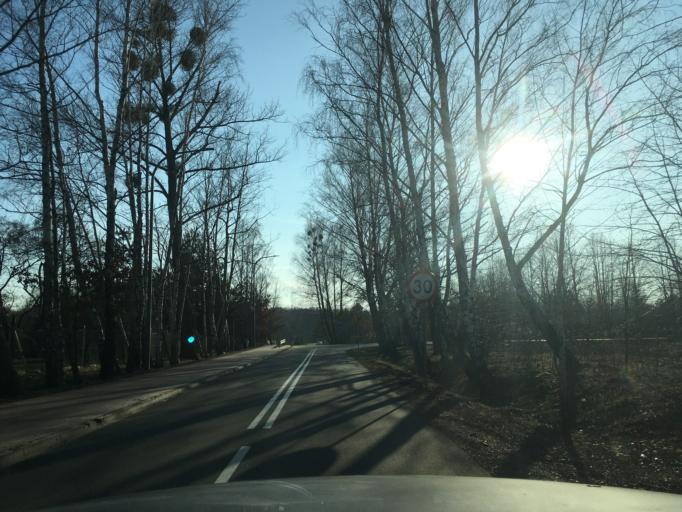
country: PL
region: Masovian Voivodeship
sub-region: Powiat pruszkowski
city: Nadarzyn
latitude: 52.0485
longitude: 20.7665
